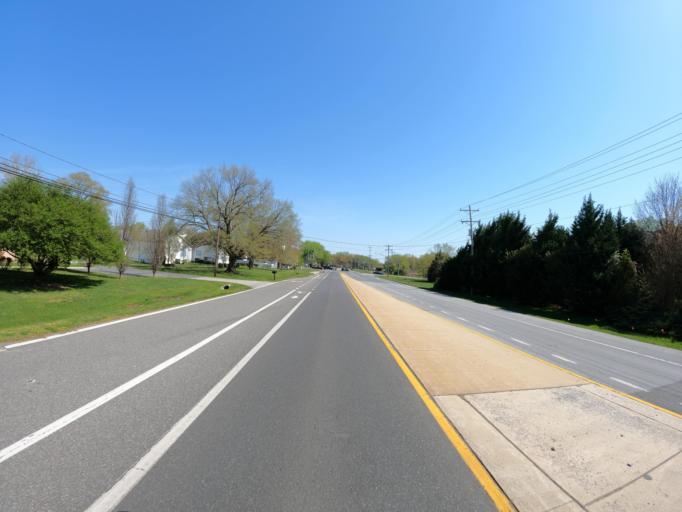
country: US
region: Delaware
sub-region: New Castle County
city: Glasgow
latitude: 39.6273
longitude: -75.7737
